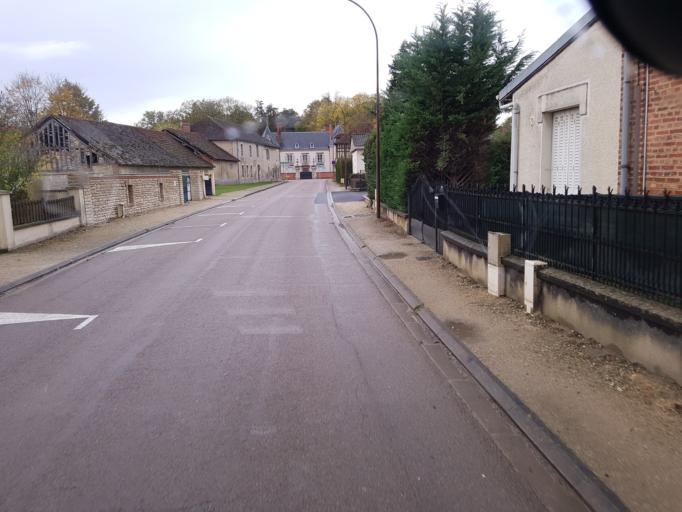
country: FR
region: Champagne-Ardenne
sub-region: Departement de l'Aube
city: Lusigny-sur-Barse
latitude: 48.2529
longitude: 4.2635
